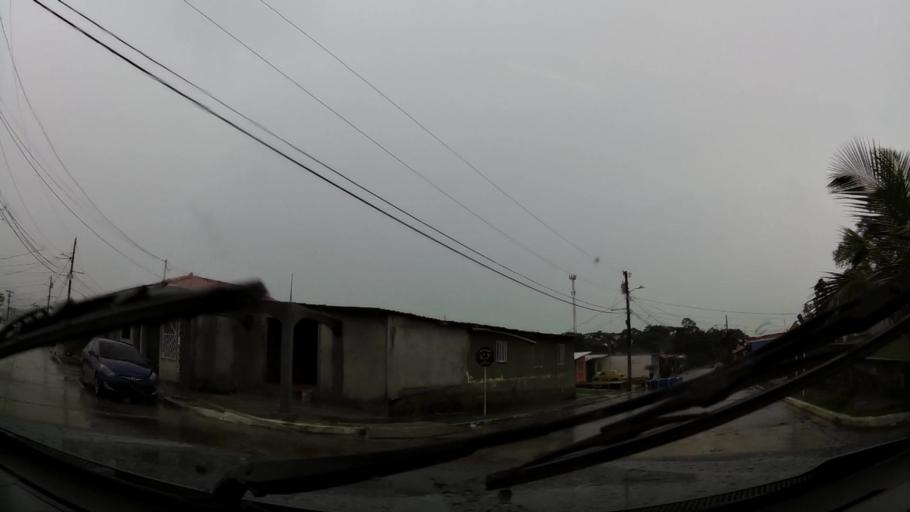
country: PA
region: Colon
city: Puerto Pilon
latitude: 9.3569
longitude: -79.7888
